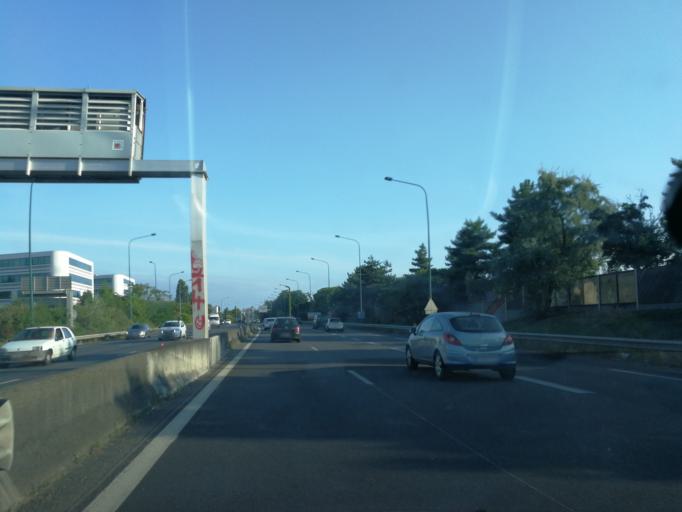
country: FR
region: Midi-Pyrenees
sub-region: Departement de la Haute-Garonne
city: Blagnac
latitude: 43.6289
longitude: 1.3833
